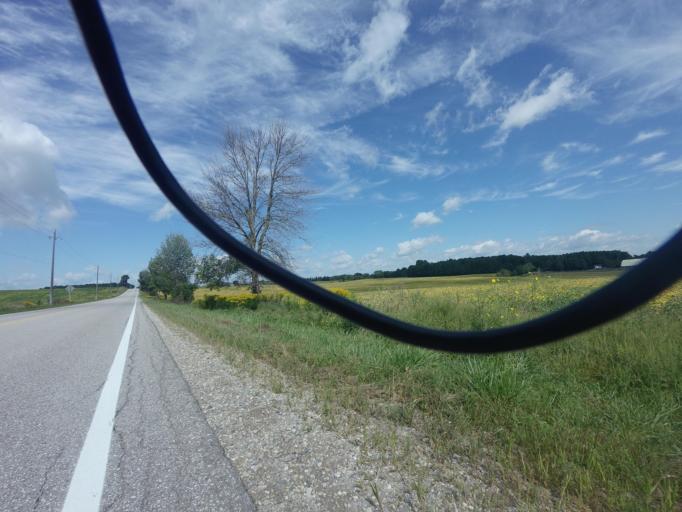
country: CA
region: Ontario
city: Stratford
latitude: 43.4886
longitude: -80.7769
